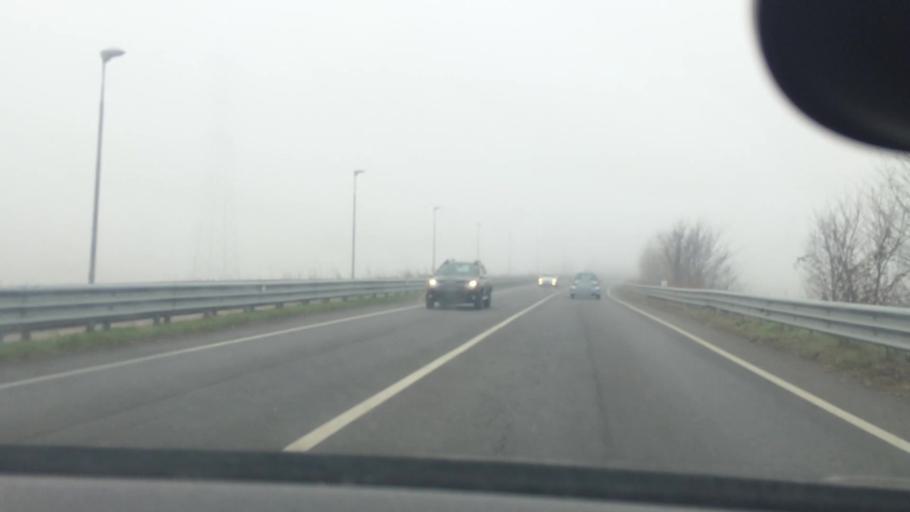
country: IT
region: Lombardy
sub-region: Provincia di Monza e Brianza
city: Ceriano Laghetto
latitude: 45.6196
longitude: 9.0606
